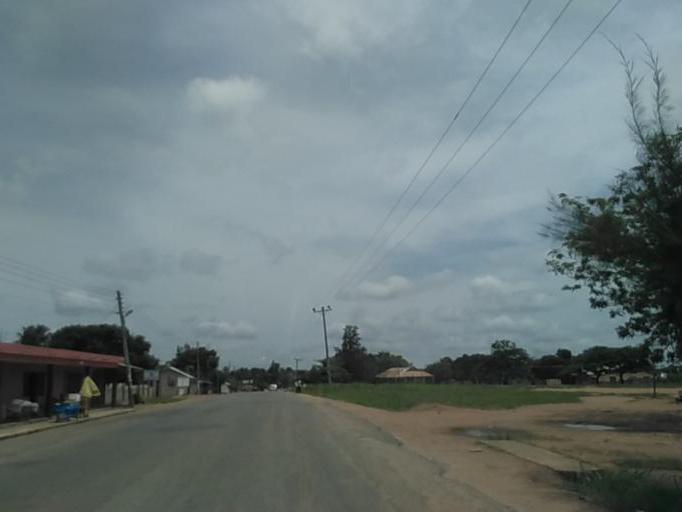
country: GH
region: Ashanti
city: Mamponteng
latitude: 6.8295
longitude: -1.4992
